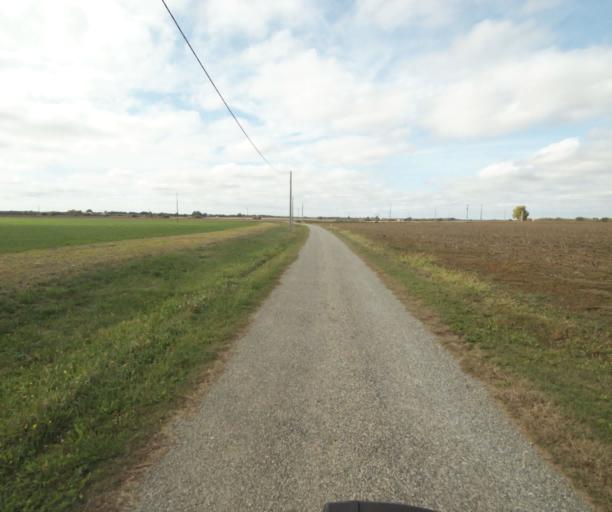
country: FR
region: Midi-Pyrenees
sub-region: Departement du Tarn-et-Garonne
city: Saint-Porquier
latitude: 43.9572
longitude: 1.1644
